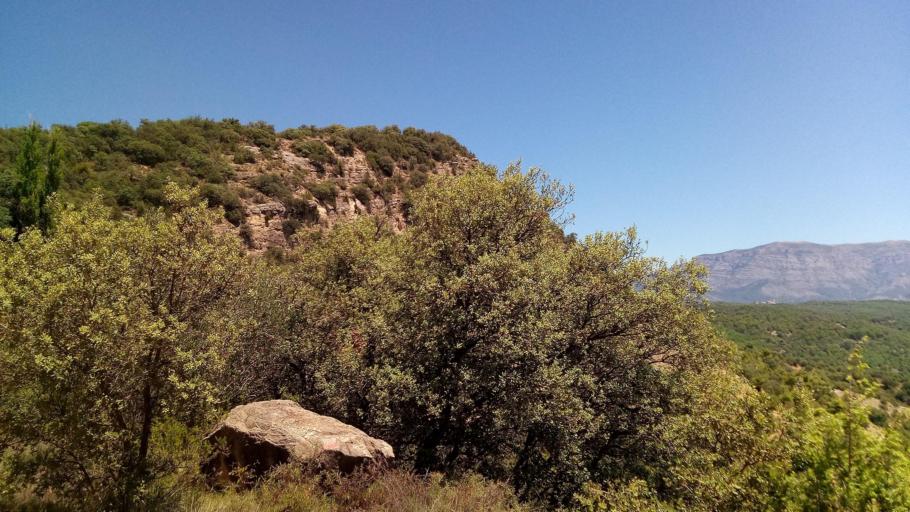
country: ES
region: Aragon
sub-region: Provincia de Huesca
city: Lascuarre
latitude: 42.2671
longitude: 0.4883
